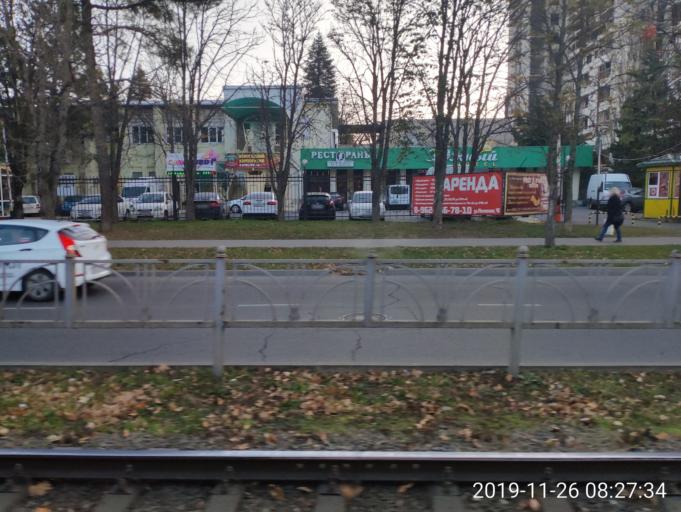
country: RU
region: Krasnodarskiy
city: Krasnodar
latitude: 45.0564
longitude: 39.0025
